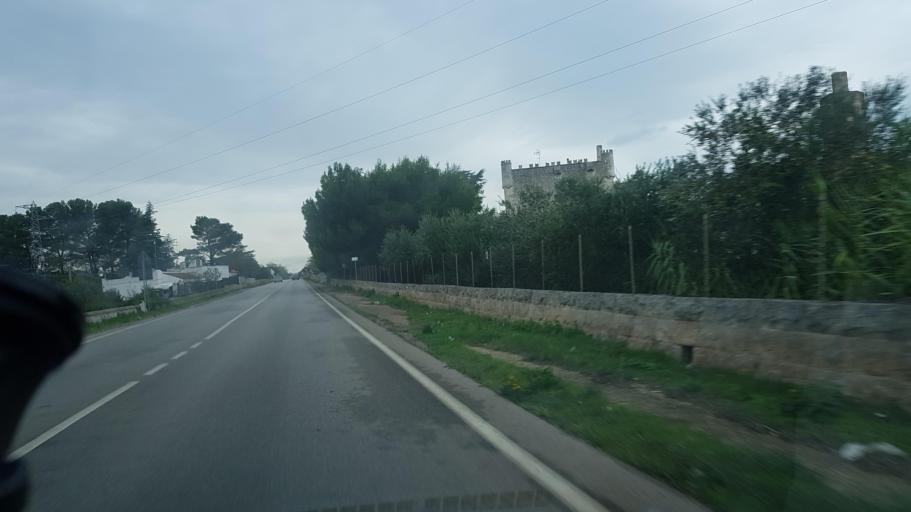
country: IT
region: Apulia
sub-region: Provincia di Brindisi
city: Ostuni
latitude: 40.7192
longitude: 17.6105
